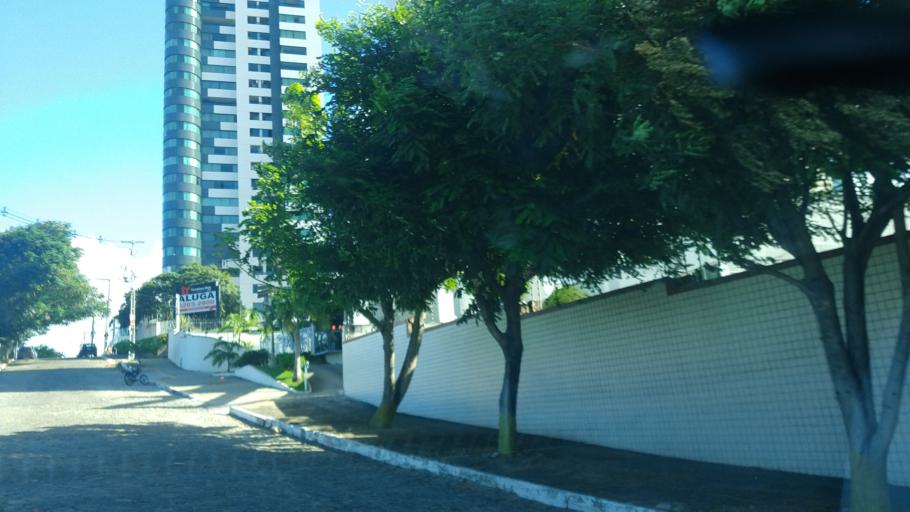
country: BR
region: Rio Grande do Norte
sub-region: Natal
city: Natal
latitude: -5.8293
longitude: -35.2181
